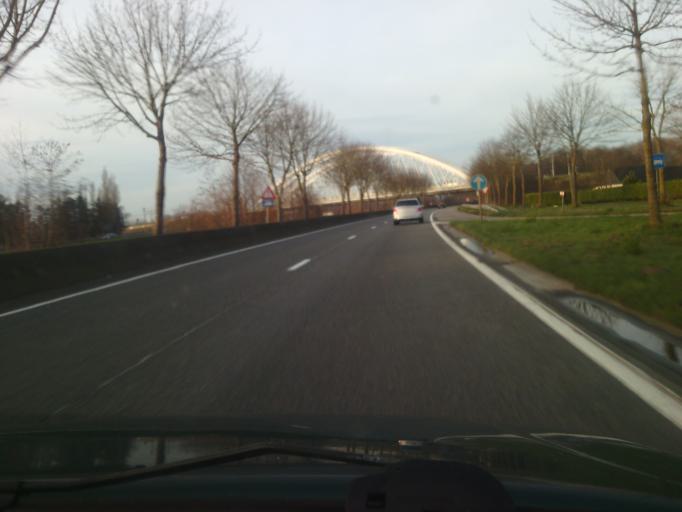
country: BE
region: Flanders
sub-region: Provincie Oost-Vlaanderen
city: Gent
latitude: 51.0395
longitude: 3.6809
